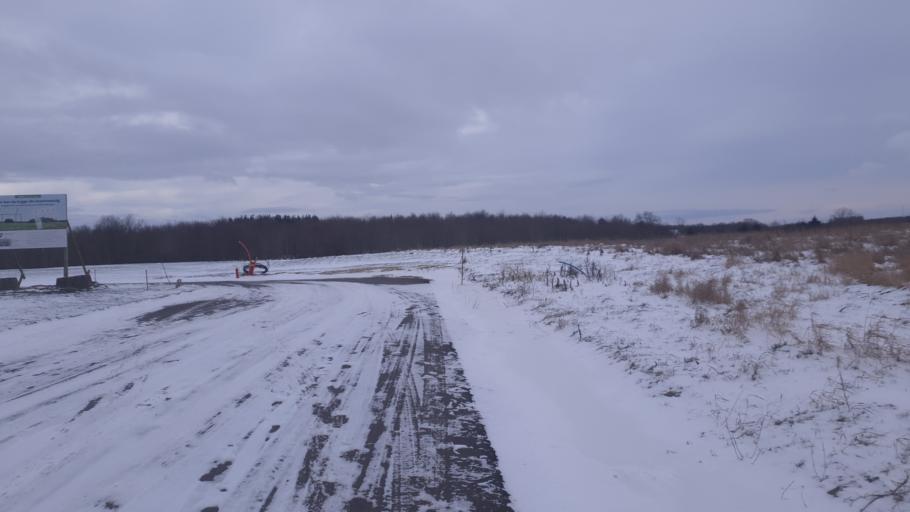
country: DK
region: Central Jutland
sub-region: Hedensted Kommune
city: Hedensted
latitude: 55.8014
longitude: 9.7065
